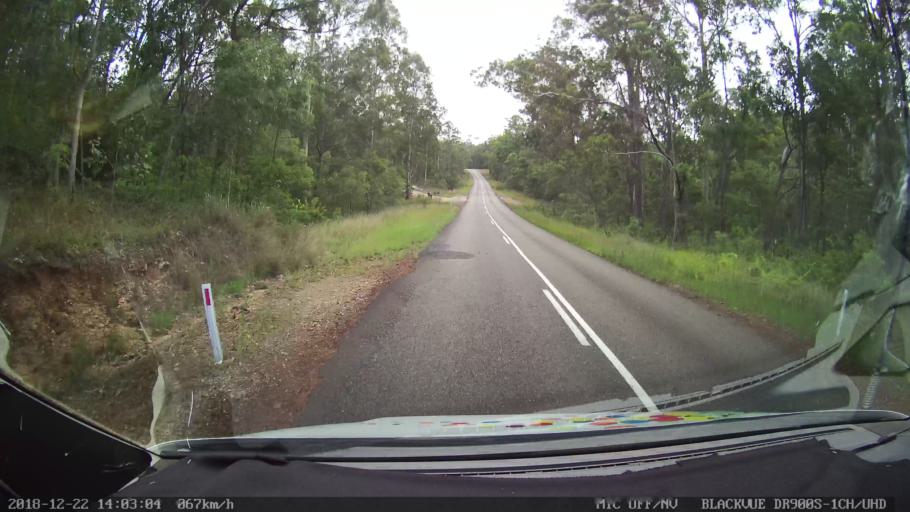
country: AU
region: New South Wales
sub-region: Clarence Valley
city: Coutts Crossing
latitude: -29.9272
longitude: 152.7424
